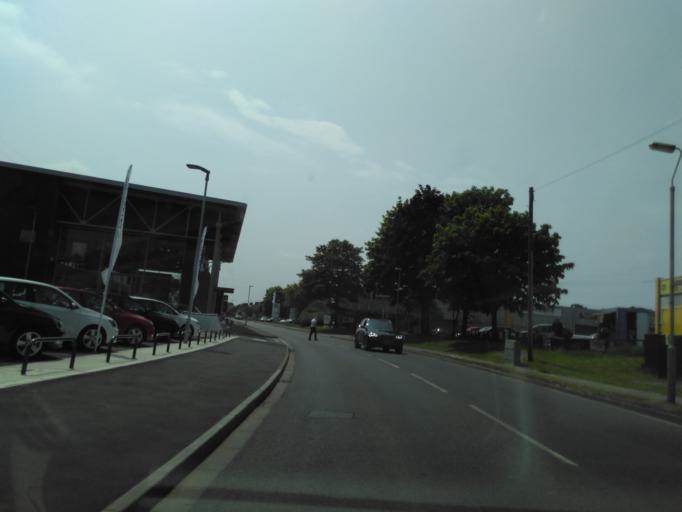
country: GB
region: England
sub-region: Kent
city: Canterbury
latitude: 51.2927
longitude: 1.0915
